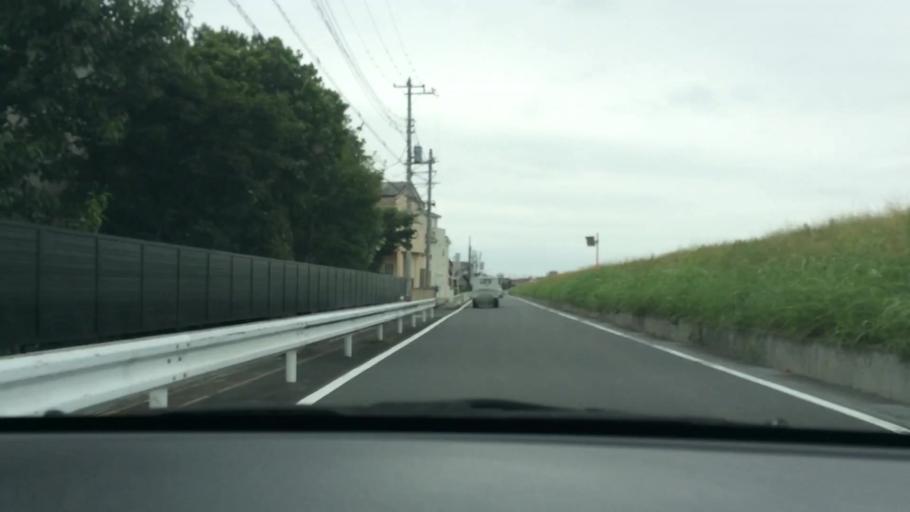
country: JP
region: Chiba
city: Matsudo
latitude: 35.7893
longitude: 139.8874
